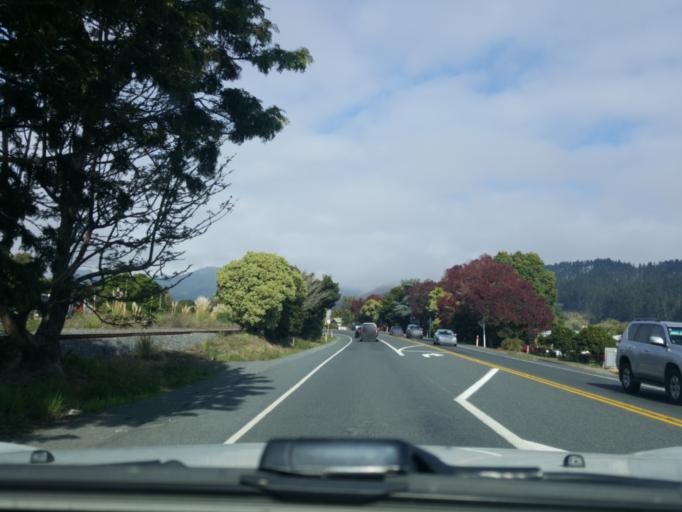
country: NZ
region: Waikato
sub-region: Waikato District
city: Ngaruawahia
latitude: -37.5795
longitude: 175.1594
